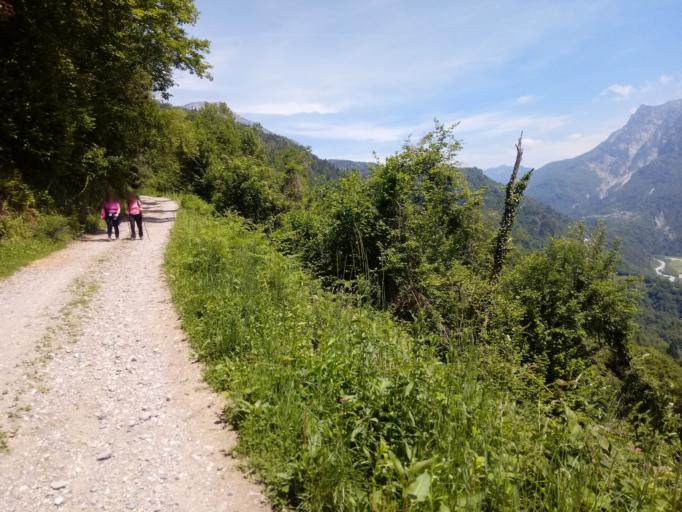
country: IT
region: Friuli Venezia Giulia
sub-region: Provincia di Udine
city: Zuglio
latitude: 46.4693
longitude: 13.0486
